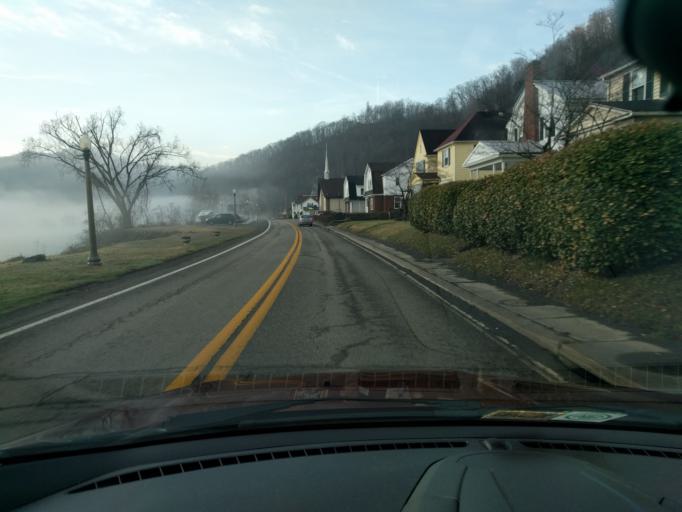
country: US
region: West Virginia
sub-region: Kanawha County
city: Montgomery
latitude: 38.1539
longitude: -81.2150
